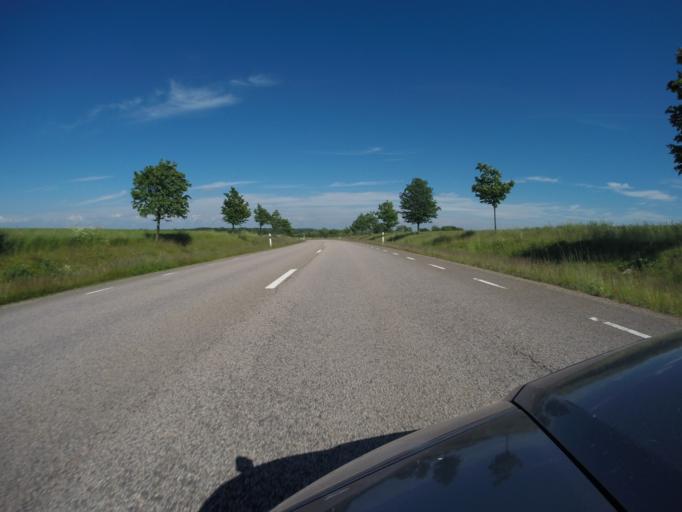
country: SE
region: Skane
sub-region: Bjuvs Kommun
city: Billesholm
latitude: 56.0111
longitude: 12.9421
